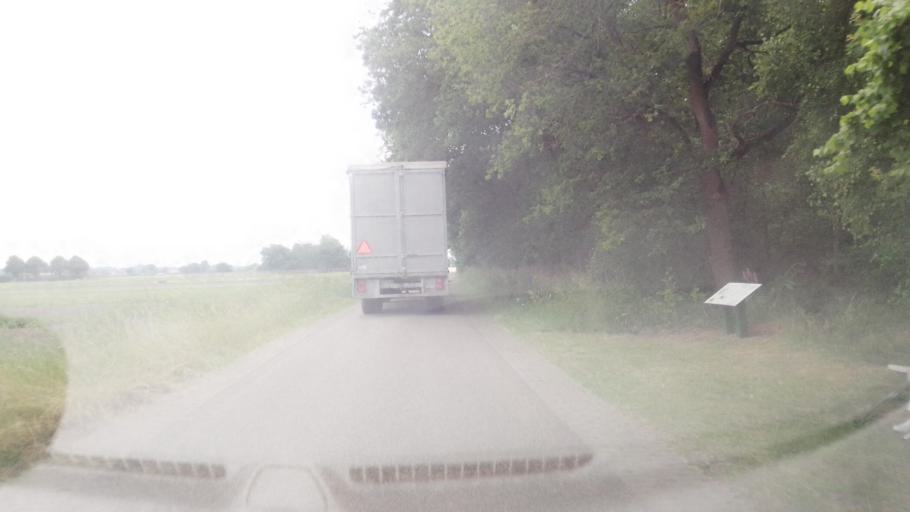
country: NL
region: Limburg
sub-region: Gemeente Peel en Maas
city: Maasbree
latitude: 51.4017
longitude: 6.0072
